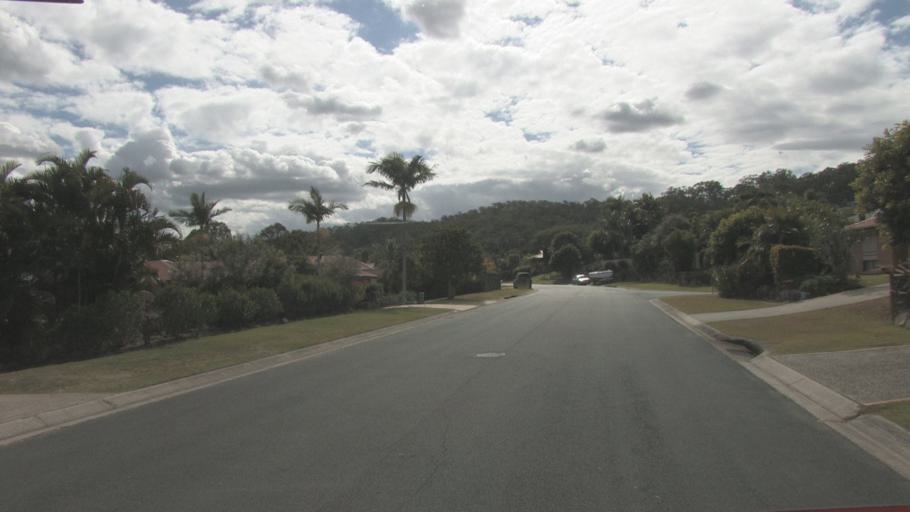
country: AU
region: Queensland
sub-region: Logan
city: Windaroo
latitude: -27.7372
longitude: 153.2007
